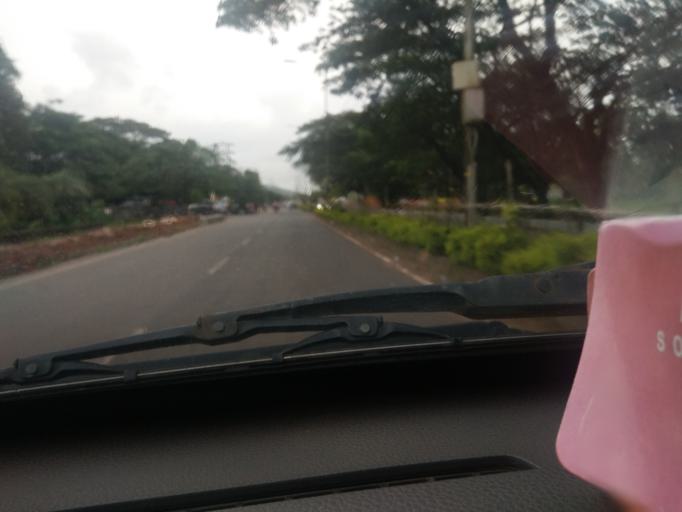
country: IN
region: Goa
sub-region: South Goa
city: Madgaon
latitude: 15.2843
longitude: 73.9590
